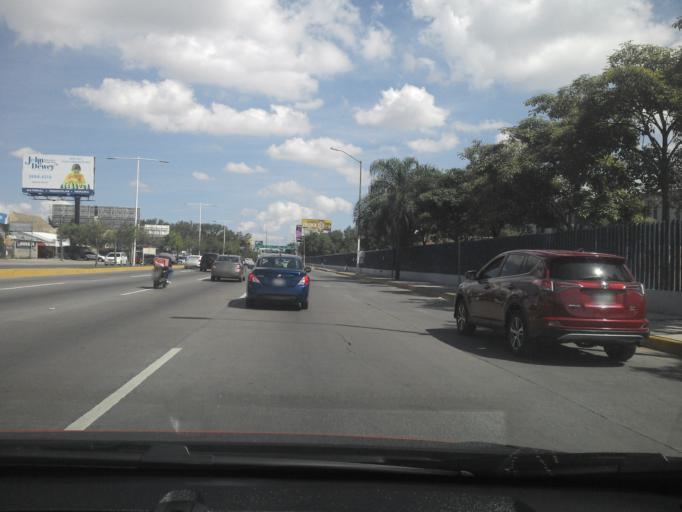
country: MX
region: Jalisco
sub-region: Tlajomulco de Zuniga
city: La Tijera
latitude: 20.5989
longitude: -103.4369
